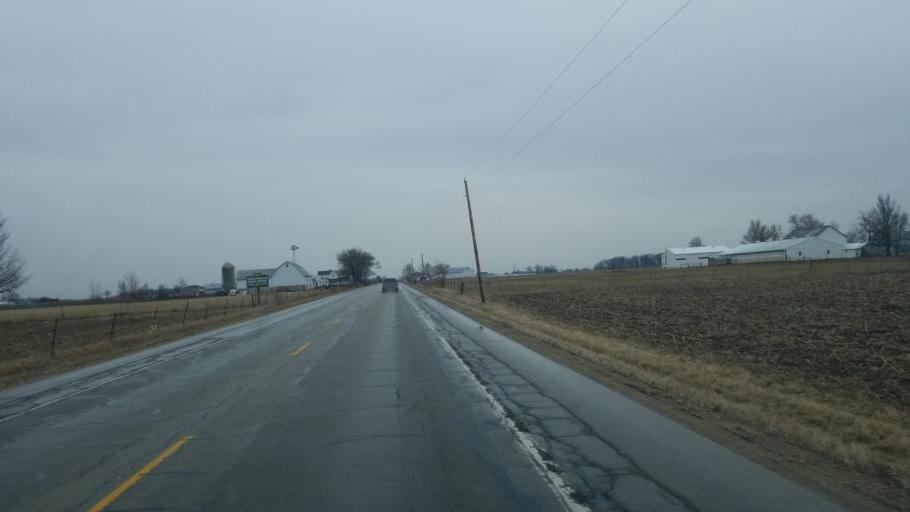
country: US
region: Indiana
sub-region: Adams County
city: Berne
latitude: 40.7241
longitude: -84.9560
